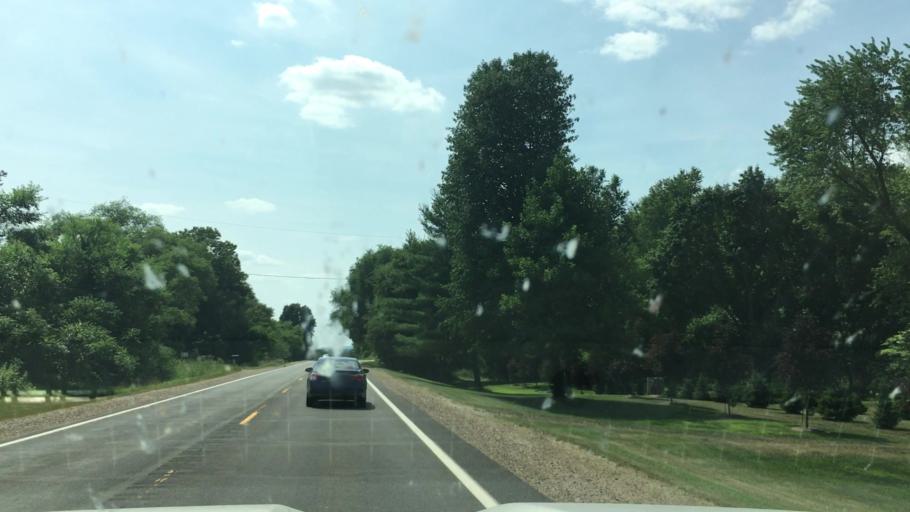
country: US
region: Michigan
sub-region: Allegan County
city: Plainwell
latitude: 42.4431
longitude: -85.5958
